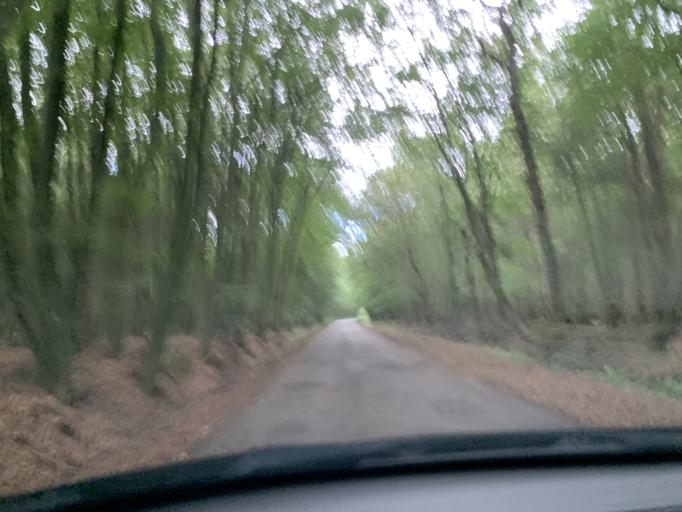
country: DE
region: Lower Saxony
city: Westerstede
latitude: 53.2696
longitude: 7.9842
